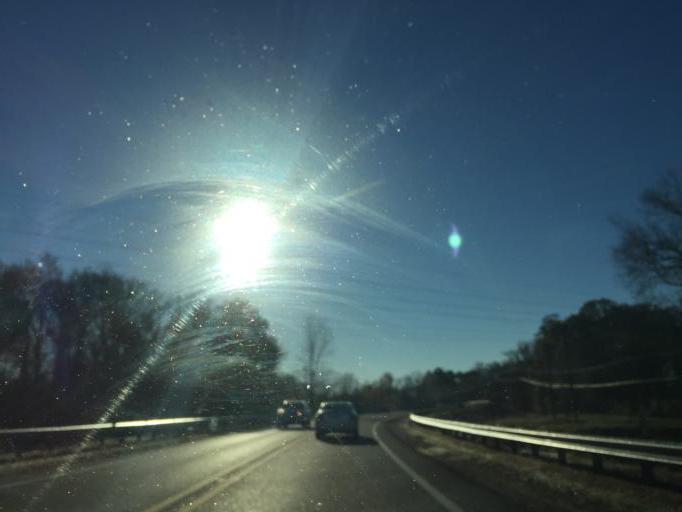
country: US
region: Mississippi
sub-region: Hinds County
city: Jackson
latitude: 32.2875
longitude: -90.1755
